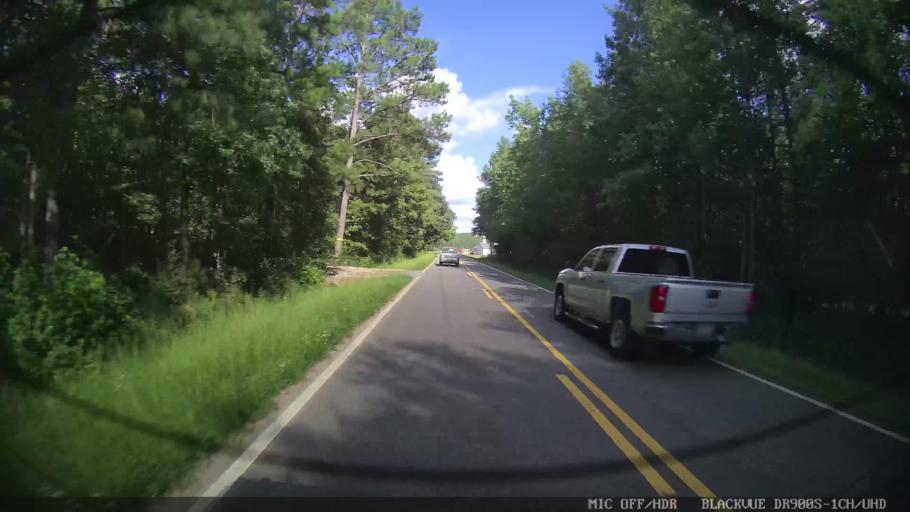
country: US
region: Georgia
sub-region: Bartow County
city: Euharlee
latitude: 34.1818
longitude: -85.0379
